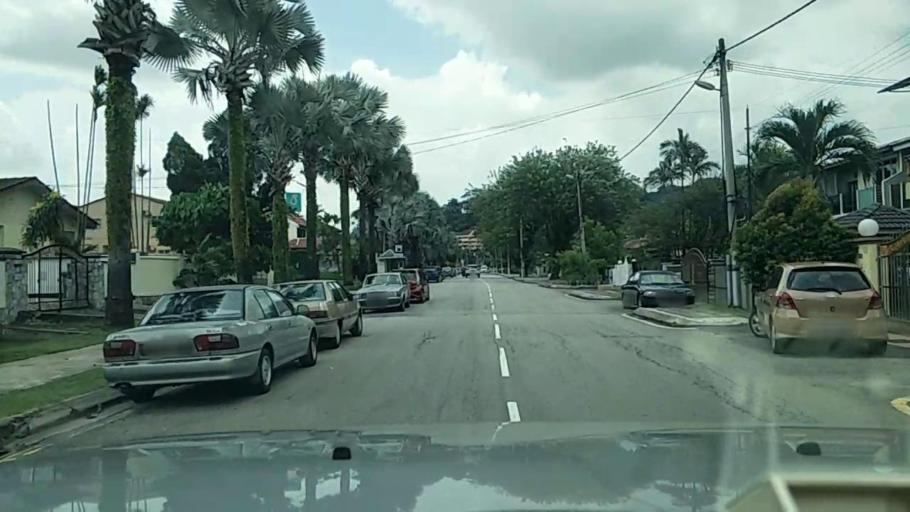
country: MY
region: Kuala Lumpur
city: Kuala Lumpur
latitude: 3.1350
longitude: 101.6734
